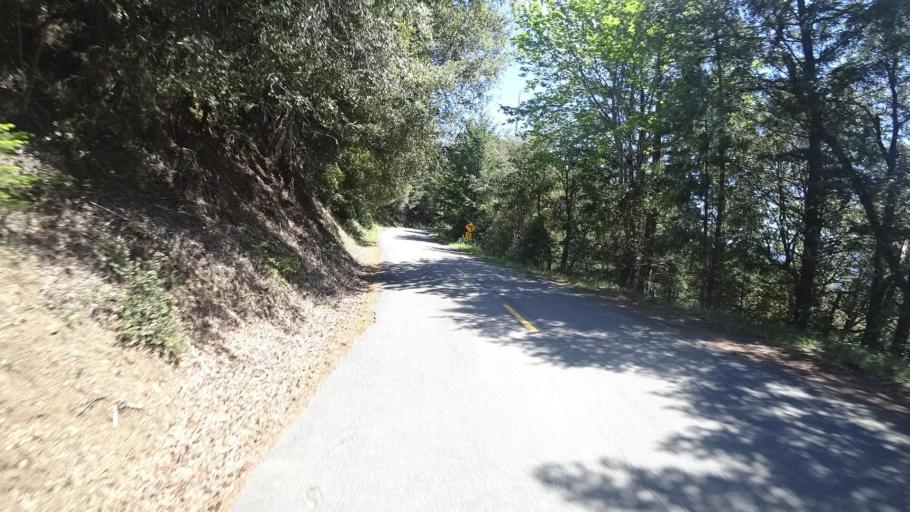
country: US
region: California
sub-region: Humboldt County
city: Rio Dell
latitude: 40.2534
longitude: -124.1189
